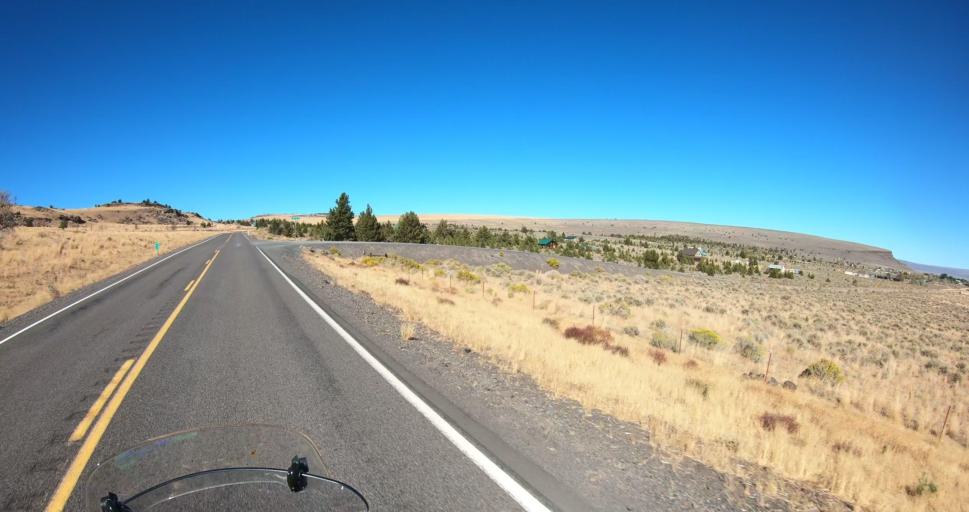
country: US
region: Oregon
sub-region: Lake County
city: Lakeview
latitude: 43.0014
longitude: -120.7762
